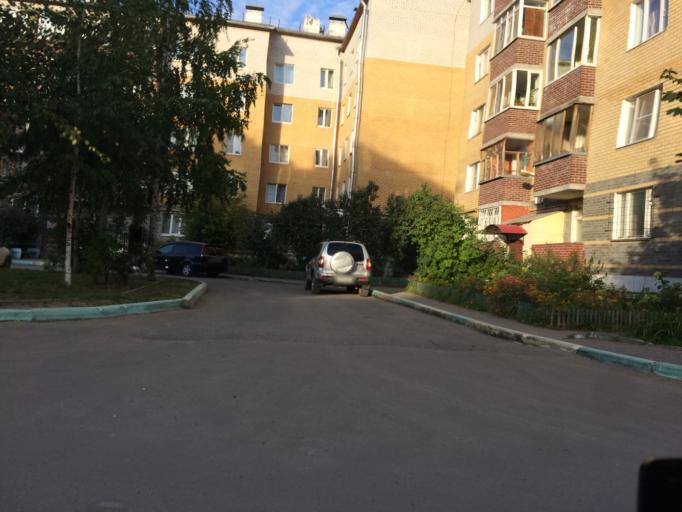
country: RU
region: Mariy-El
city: Yoshkar-Ola
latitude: 56.6295
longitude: 47.8519
